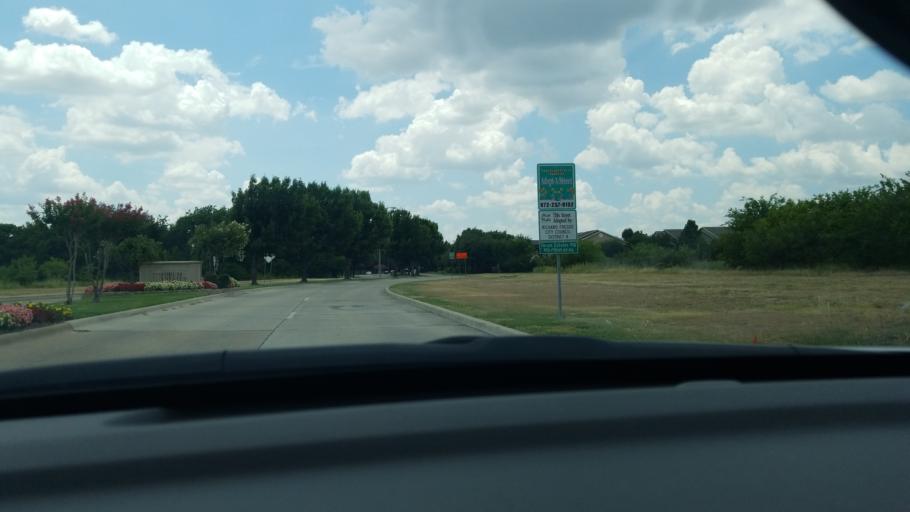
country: US
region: Texas
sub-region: Dallas County
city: Grand Prairie
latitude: 32.6841
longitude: -97.0449
